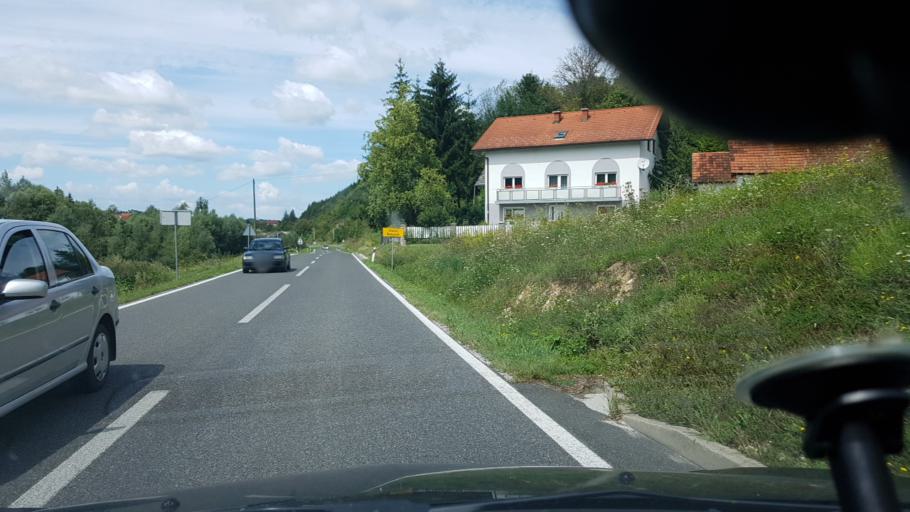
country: HR
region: Varazdinska
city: Lepoglava
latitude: 46.2172
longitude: 15.9978
